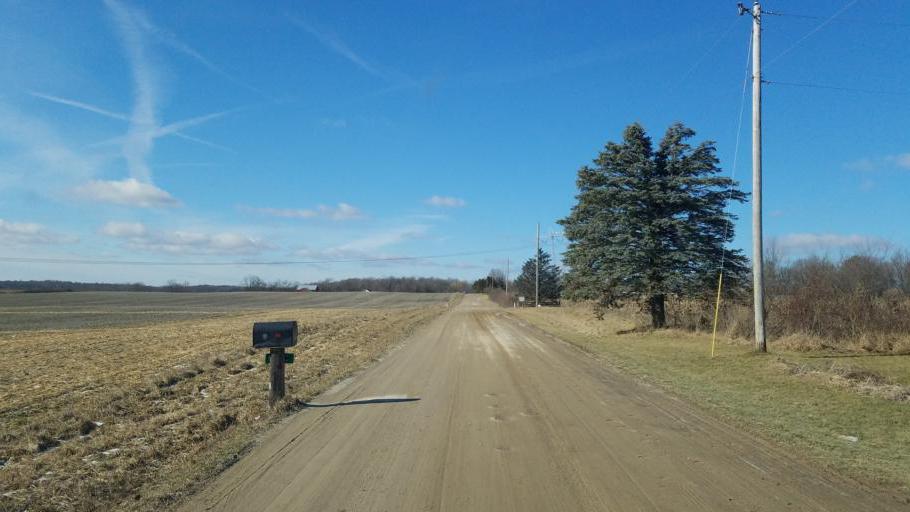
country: US
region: Ohio
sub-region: Richland County
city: Lexington
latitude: 40.5719
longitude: -82.6339
